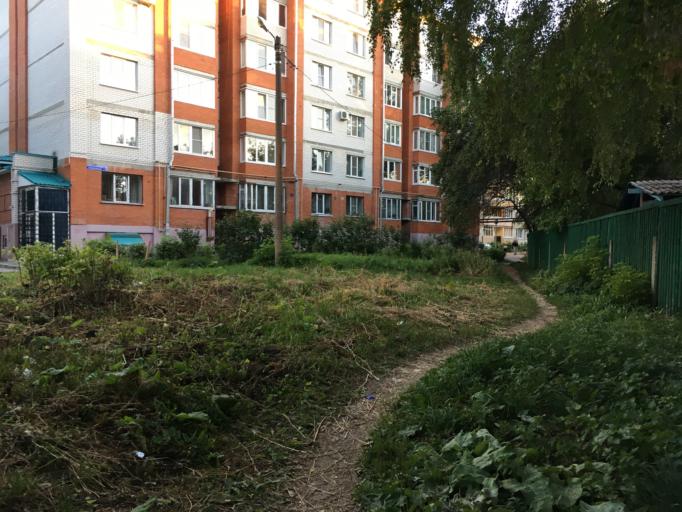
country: RU
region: Mariy-El
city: Yoshkar-Ola
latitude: 56.6491
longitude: 47.8684
